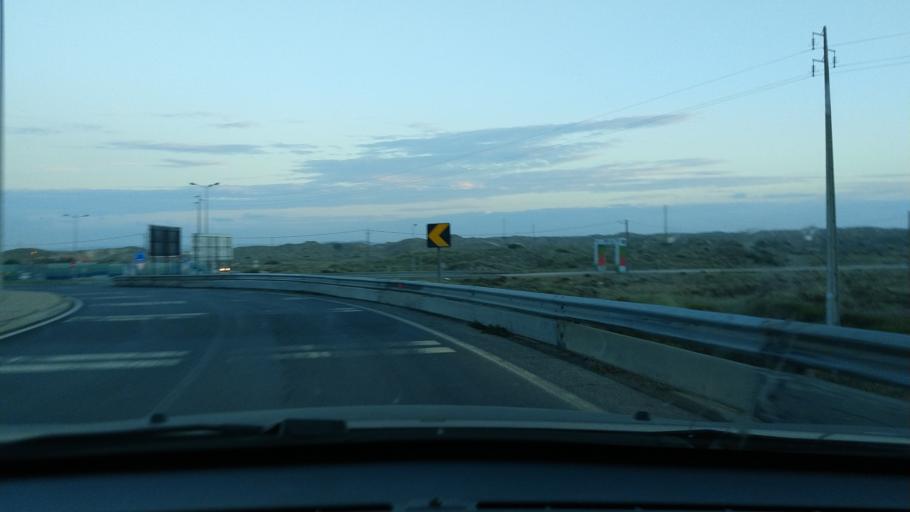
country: PT
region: Leiria
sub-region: Peniche
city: Peniche
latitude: 39.3504
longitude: -9.3611
